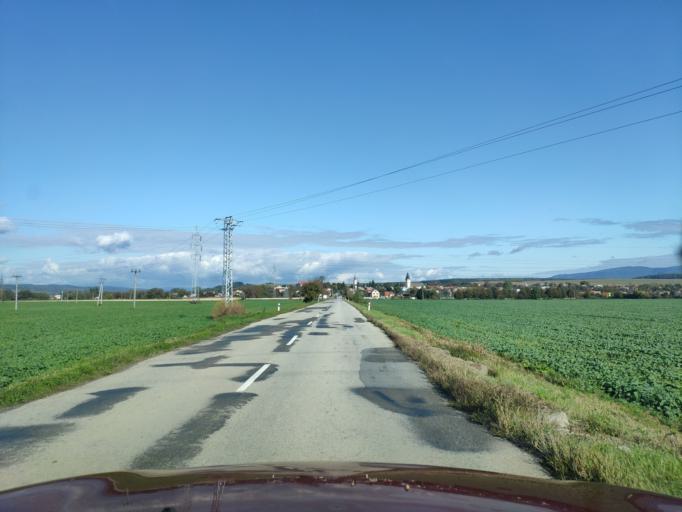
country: SK
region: Presovsky
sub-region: Okres Presov
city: Presov
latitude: 48.8633
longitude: 21.2709
